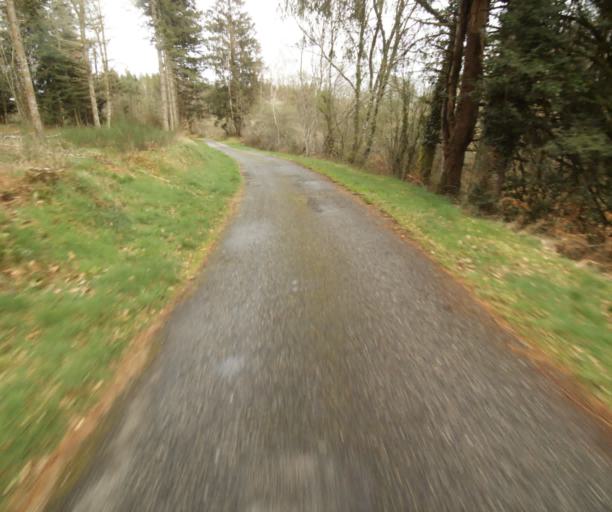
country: FR
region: Limousin
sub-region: Departement de la Correze
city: Saint-Privat
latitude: 45.2202
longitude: 2.0103
